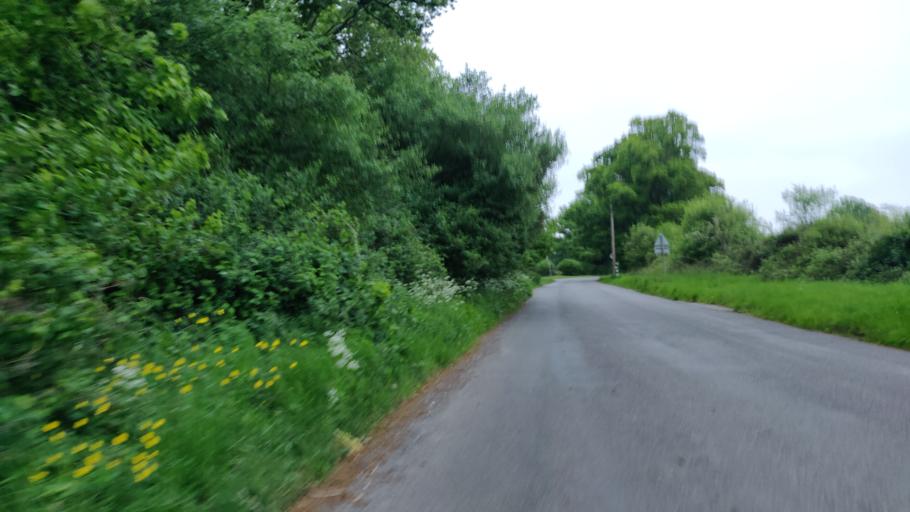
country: GB
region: England
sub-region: West Sussex
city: Southwater
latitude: 51.0135
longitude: -0.3311
